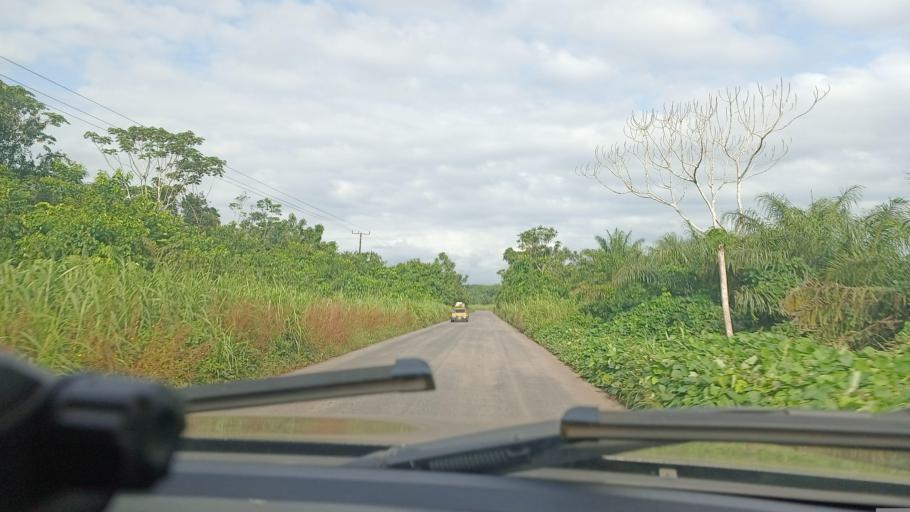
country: LR
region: Bomi
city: Tubmanburg
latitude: 6.7117
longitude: -10.9358
